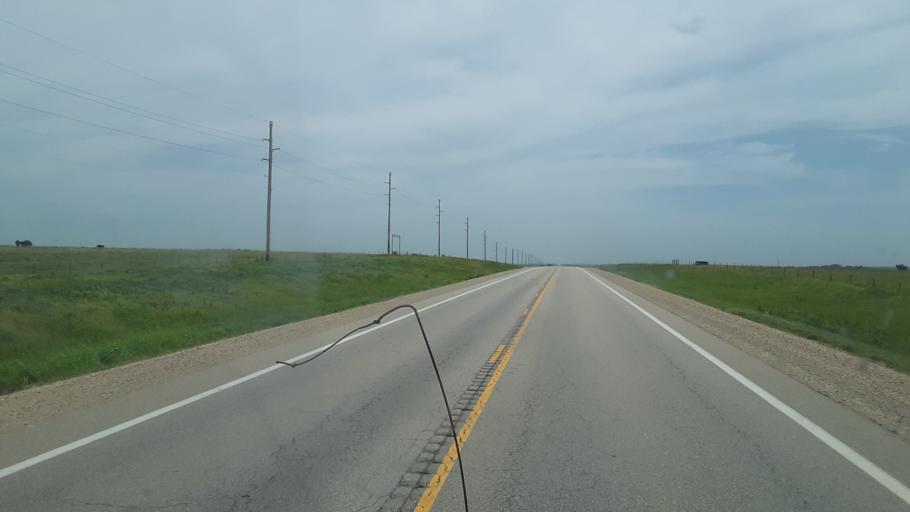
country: US
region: Kansas
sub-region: Greenwood County
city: Eureka
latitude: 37.8380
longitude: -96.1295
